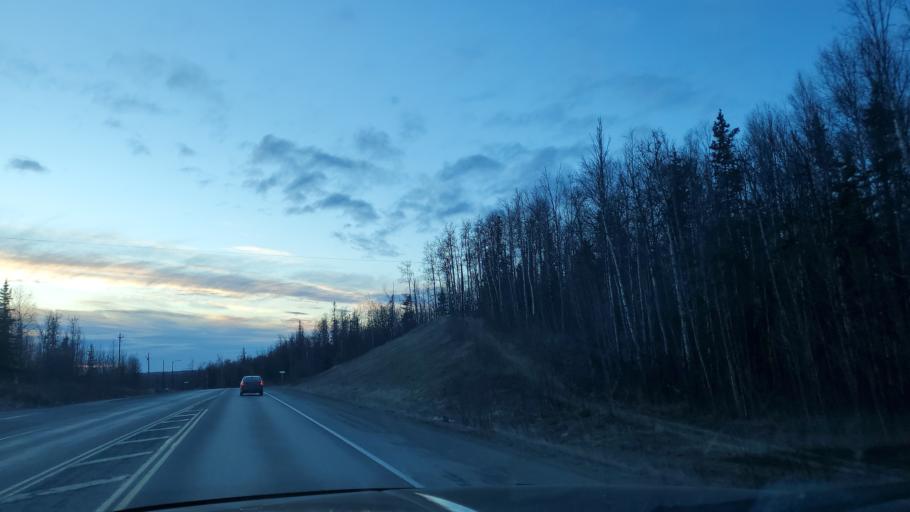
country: US
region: Alaska
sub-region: Matanuska-Susitna Borough
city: Wasilla
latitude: 61.5976
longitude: -149.4255
